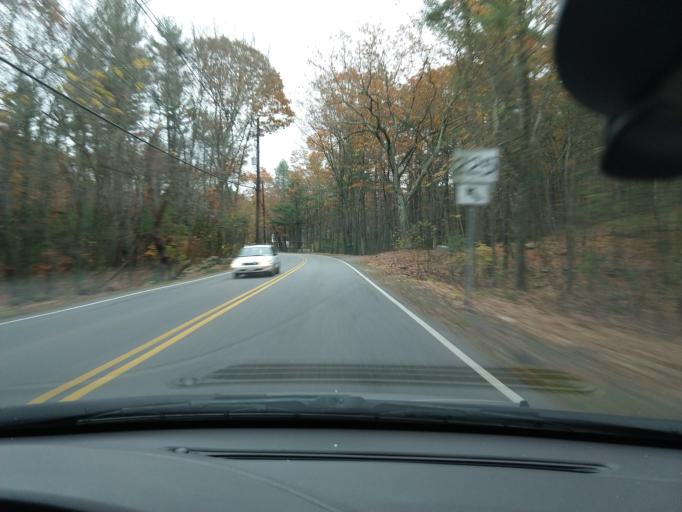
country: US
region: Massachusetts
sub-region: Middlesex County
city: Carlisle
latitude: 42.5172
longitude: -71.3251
